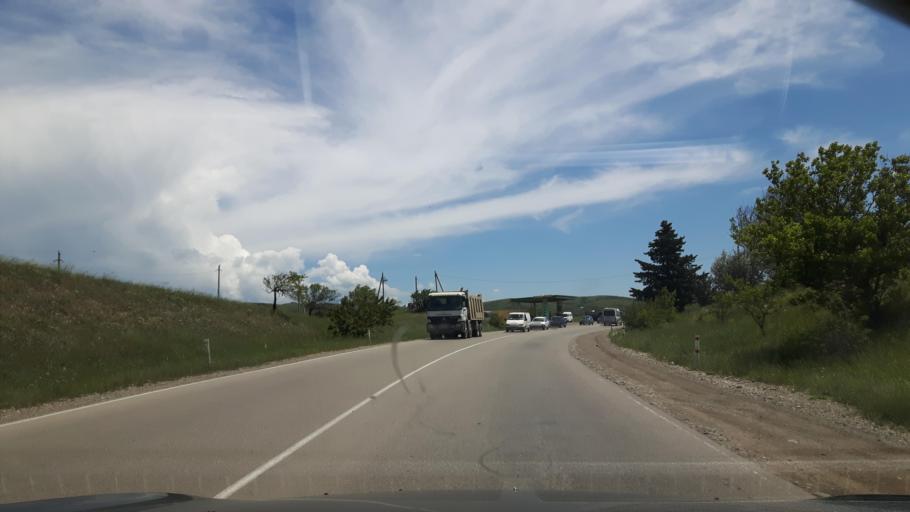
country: GE
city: Didi Lilo
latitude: 41.6980
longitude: 45.0455
